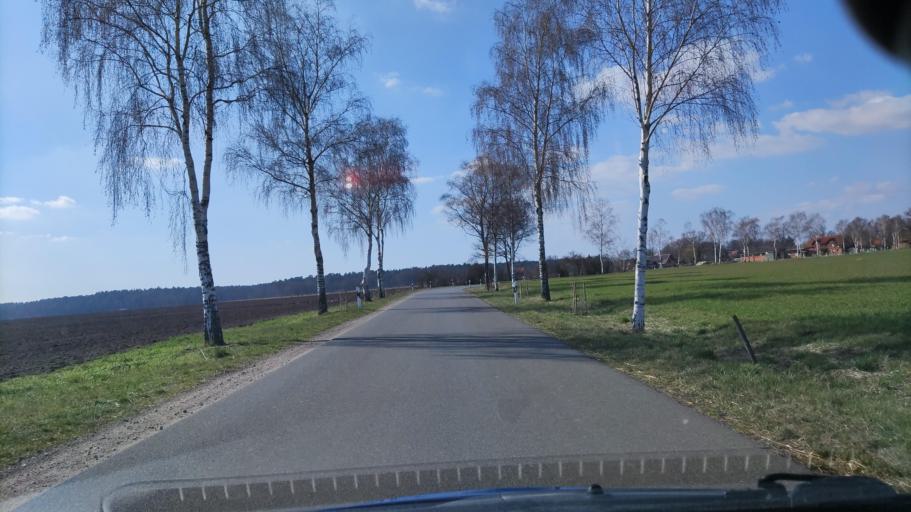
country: DE
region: Lower Saxony
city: Klein Gusborn
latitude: 53.0511
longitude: 11.2300
